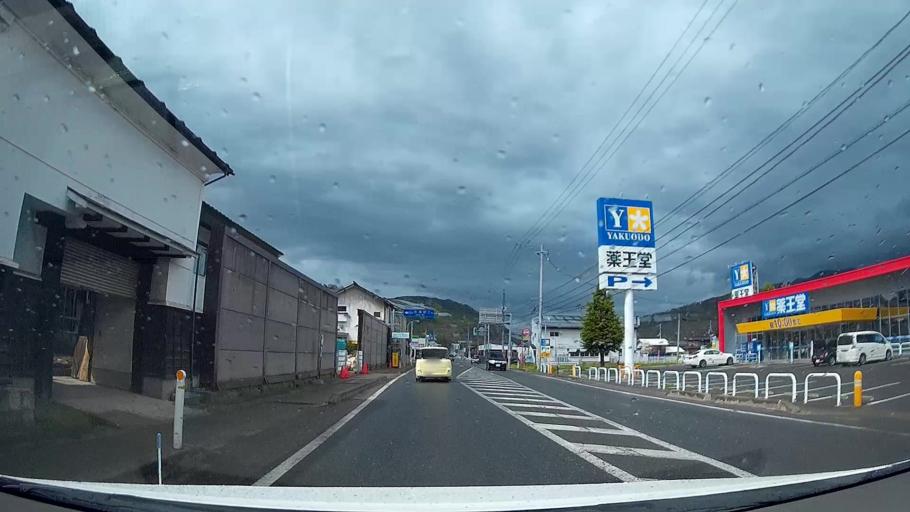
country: JP
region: Yamagata
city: Takahata
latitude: 38.0482
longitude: 140.1707
